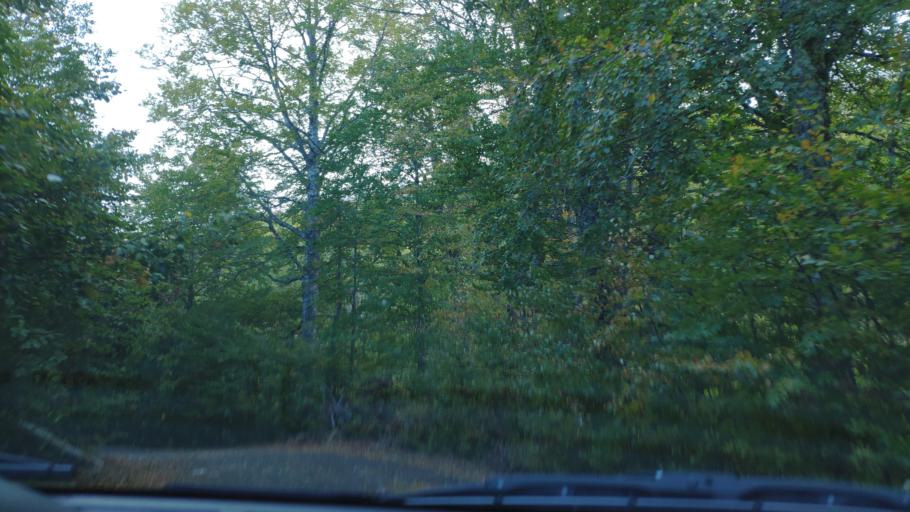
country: GR
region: West Macedonia
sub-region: Nomos Kastorias
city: Nestorio
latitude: 40.3102
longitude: 20.9152
